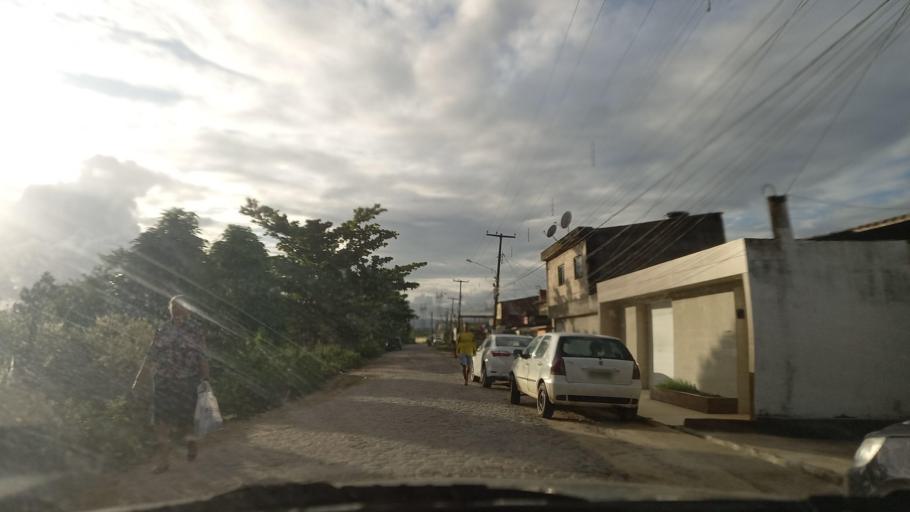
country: BR
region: Pernambuco
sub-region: Palmares
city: Palmares
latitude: -8.6800
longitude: -35.5961
